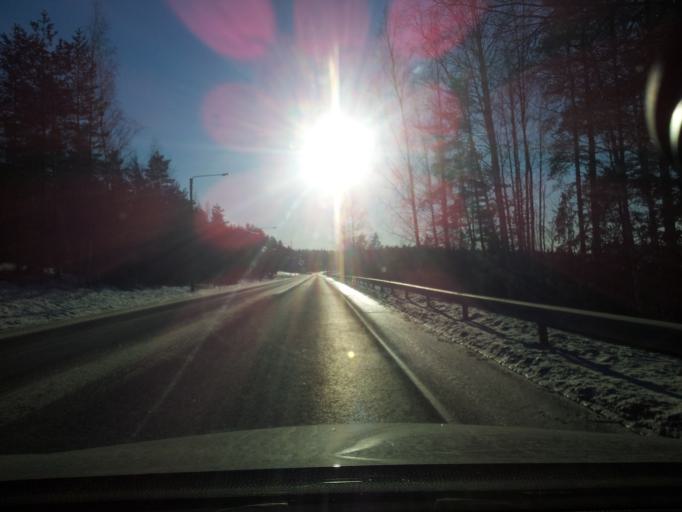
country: FI
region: Uusimaa
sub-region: Helsinki
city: Vihti
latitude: 60.3551
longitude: 24.3357
